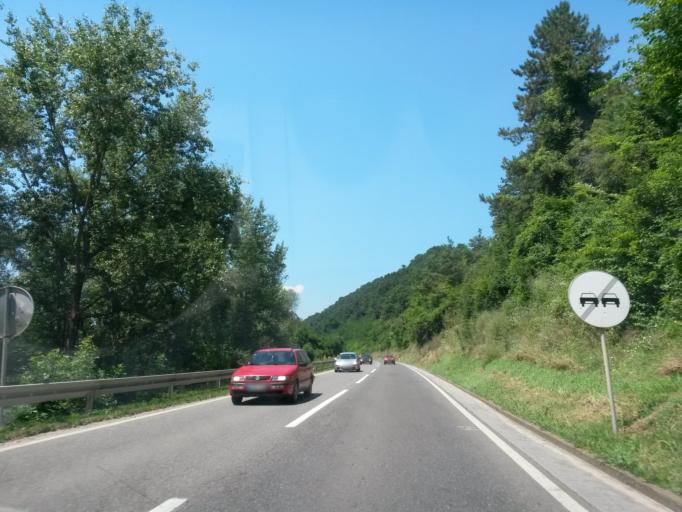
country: BA
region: Federation of Bosnia and Herzegovina
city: Odzak
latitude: 44.9704
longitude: 18.2667
